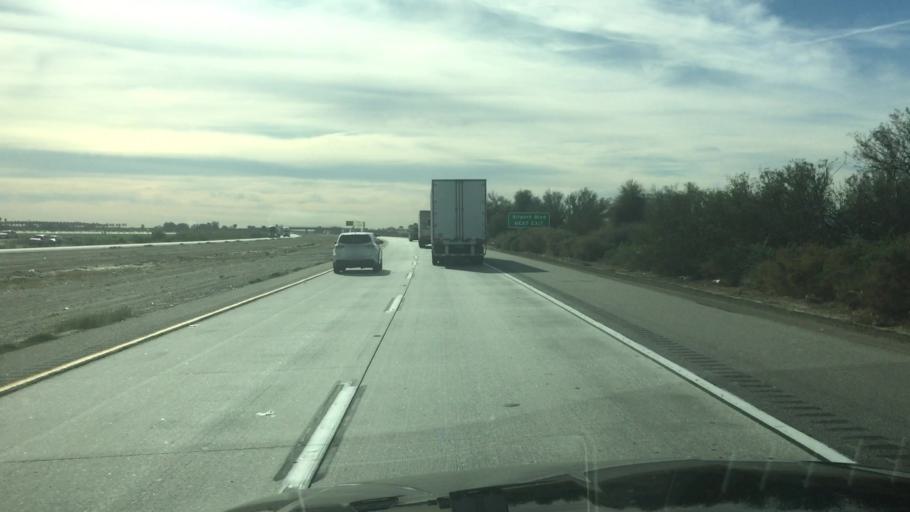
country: US
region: California
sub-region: Riverside County
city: Thermal
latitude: 33.6508
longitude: -116.1393
